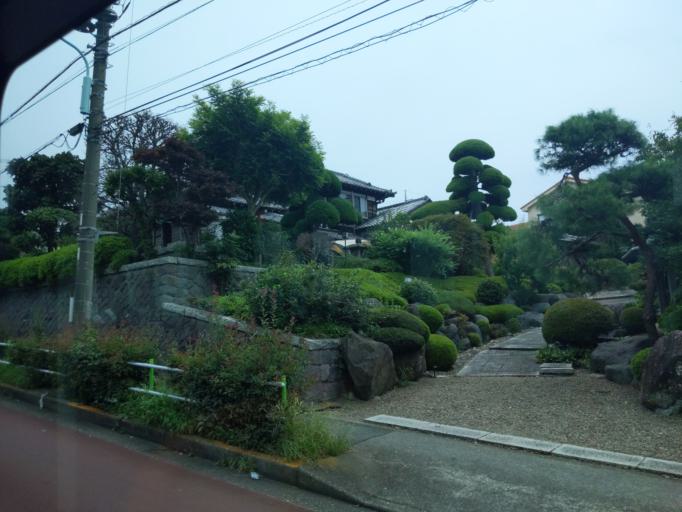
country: JP
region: Saitama
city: Wako
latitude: 35.7782
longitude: 139.6547
